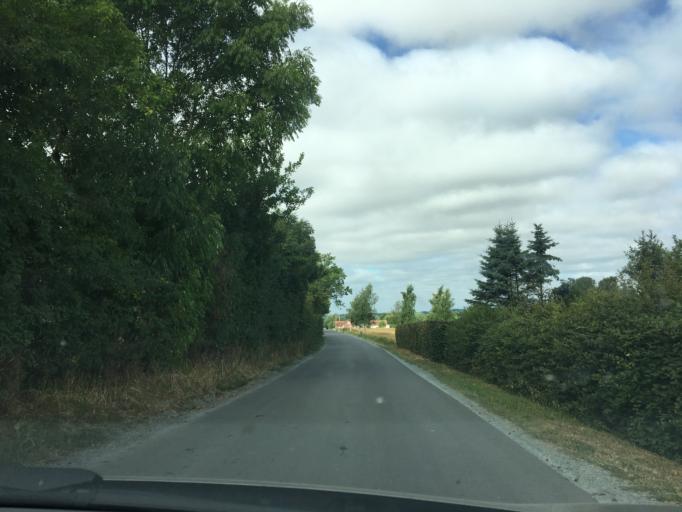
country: DK
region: South Denmark
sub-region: Middelfart Kommune
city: Norre Aby
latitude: 55.5061
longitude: 9.8895
